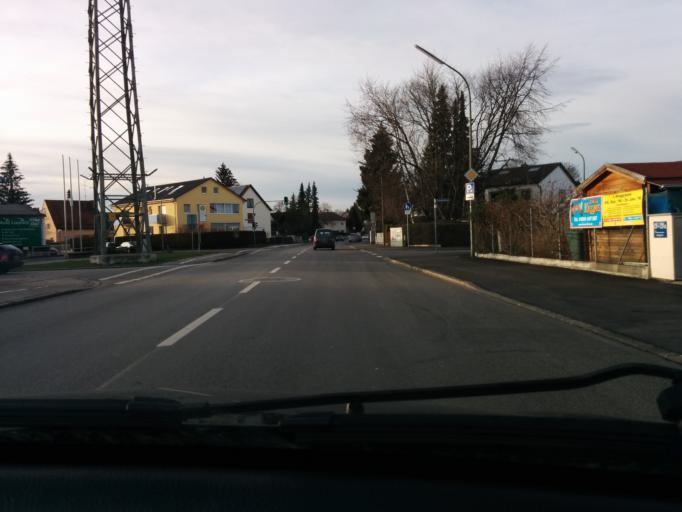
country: DE
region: Bavaria
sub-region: Upper Bavaria
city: Pasing
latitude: 48.1526
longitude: 11.4278
